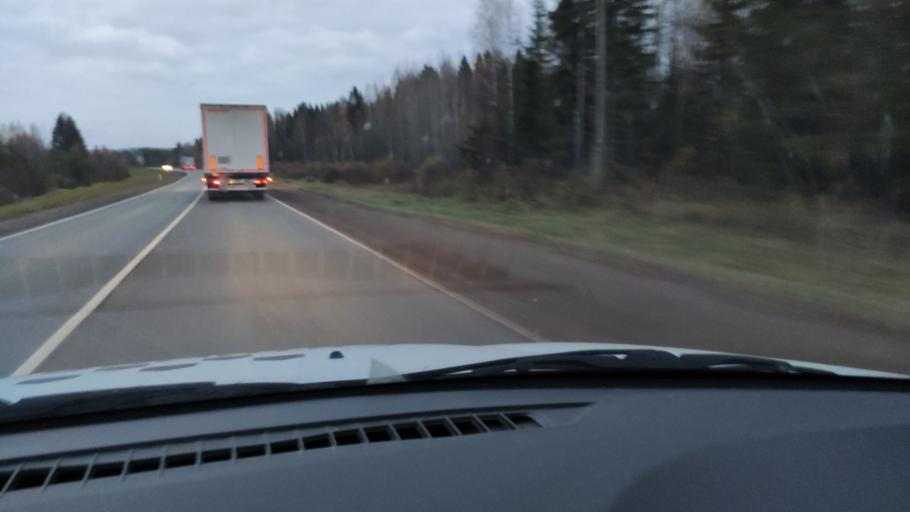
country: RU
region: Kirov
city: Kostino
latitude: 58.8558
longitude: 53.1943
